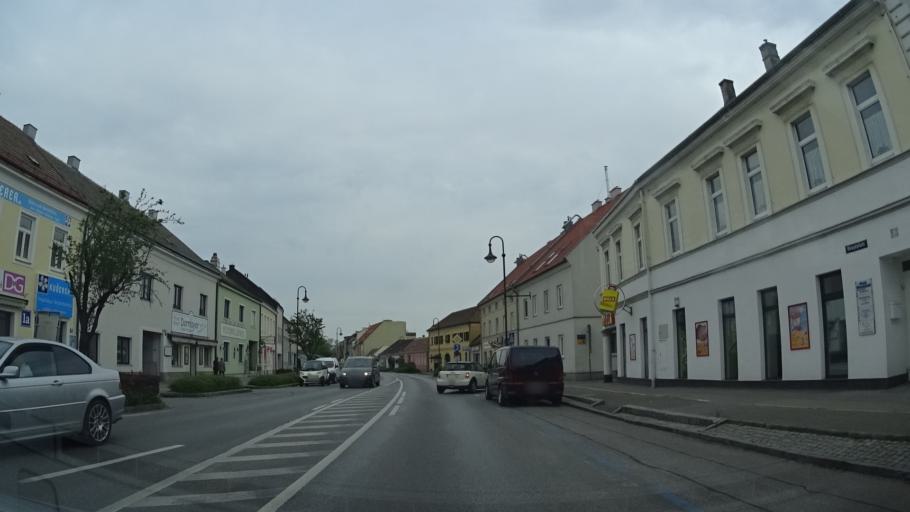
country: AT
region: Lower Austria
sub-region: Politischer Bezirk Korneuburg
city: Langenzersdorf
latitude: 48.3095
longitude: 16.3576
